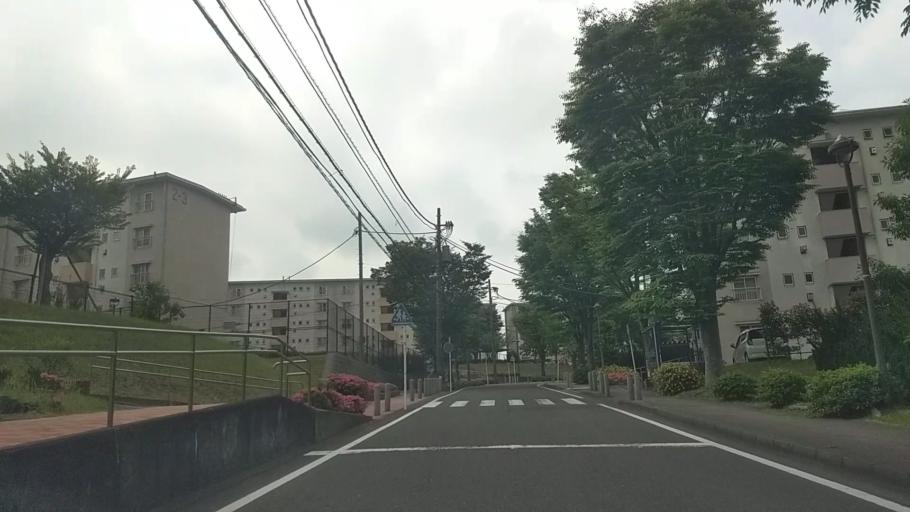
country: JP
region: Kanagawa
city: Kamakura
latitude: 35.3729
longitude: 139.5369
